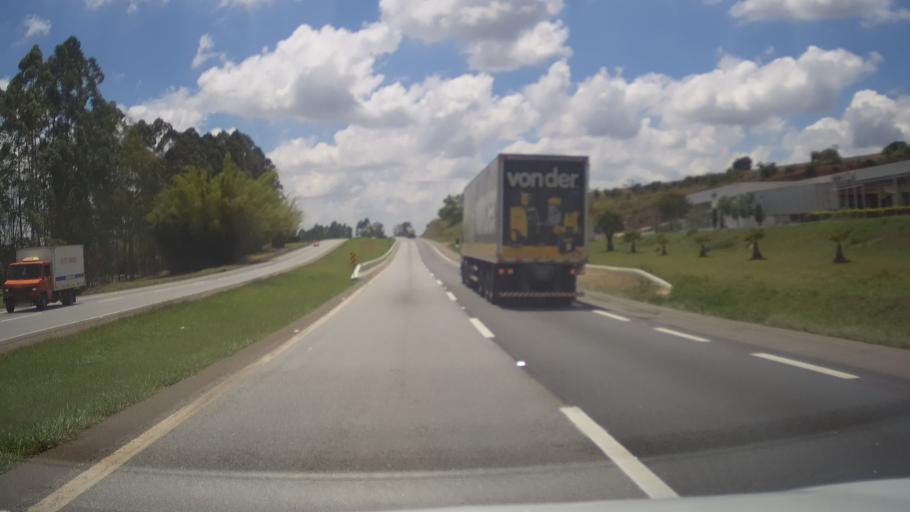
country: BR
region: Minas Gerais
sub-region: Campanha
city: Campanha
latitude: -21.7938
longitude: -45.4514
